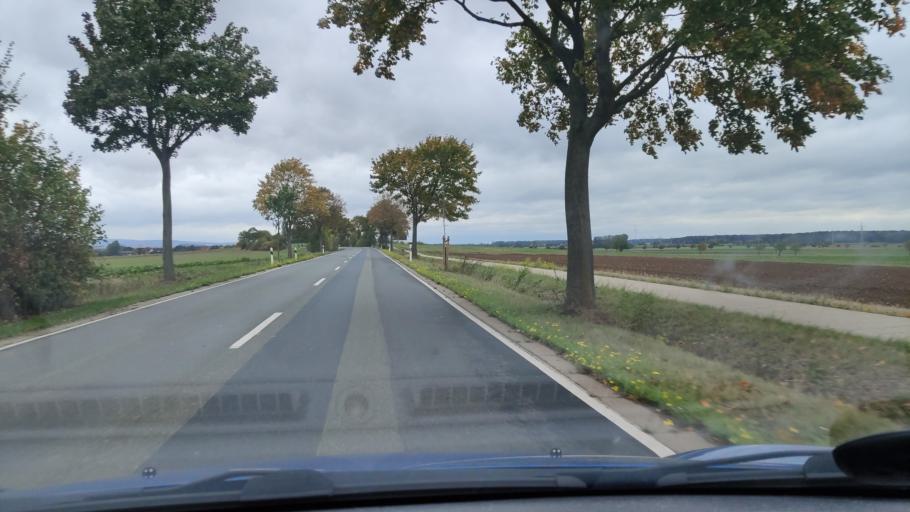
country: DE
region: Lower Saxony
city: Seelze
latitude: 52.3774
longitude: 9.6100
